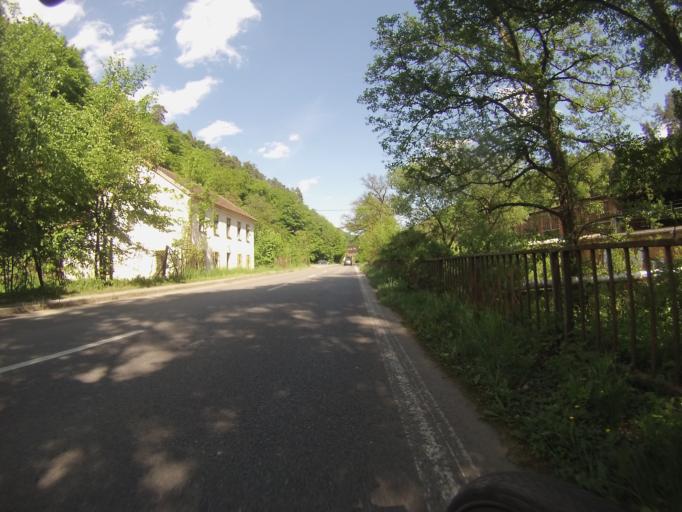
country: CZ
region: South Moravian
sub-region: Okres Blansko
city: Blansko
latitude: 49.3528
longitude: 16.6652
